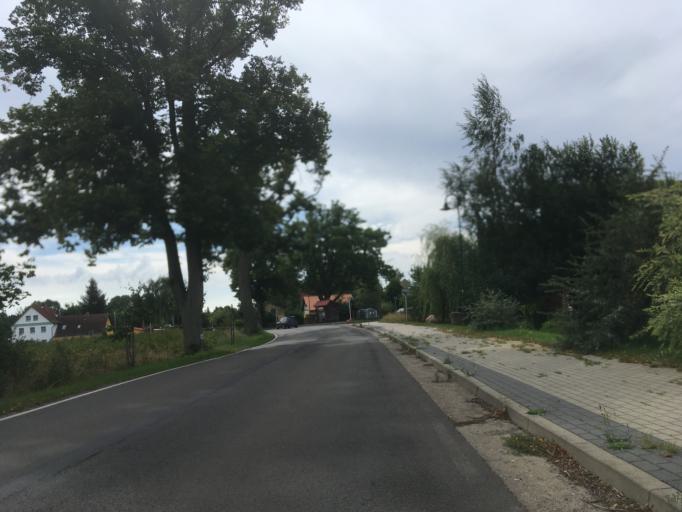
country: DE
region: Brandenburg
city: Mittenwalde
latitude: 53.2236
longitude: 13.6612
